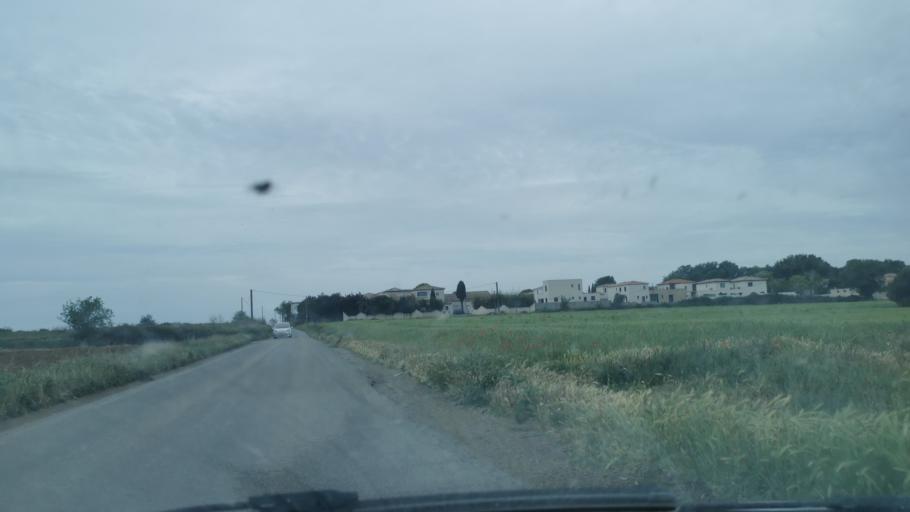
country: FR
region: Languedoc-Roussillon
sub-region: Departement de l'Herault
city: Saussan
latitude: 43.5673
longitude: 3.7803
